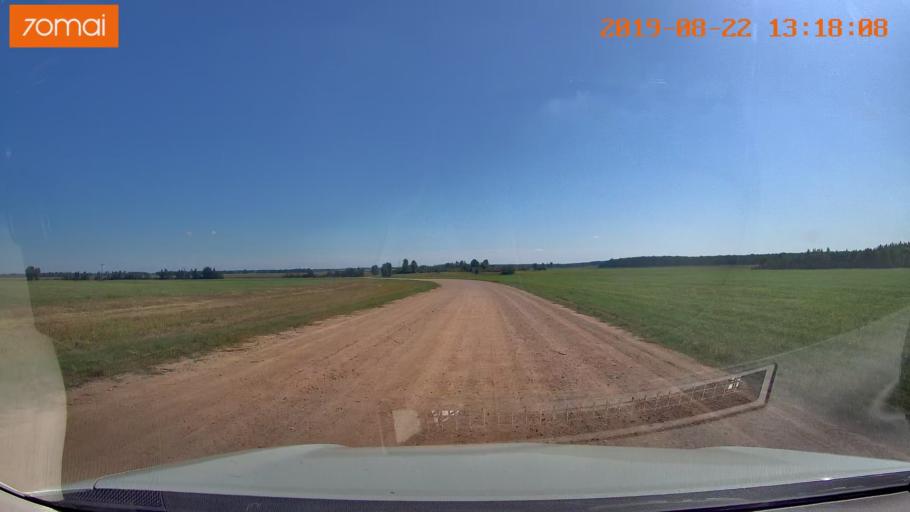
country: BY
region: Minsk
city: Urechcha
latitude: 53.2428
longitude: 27.9332
